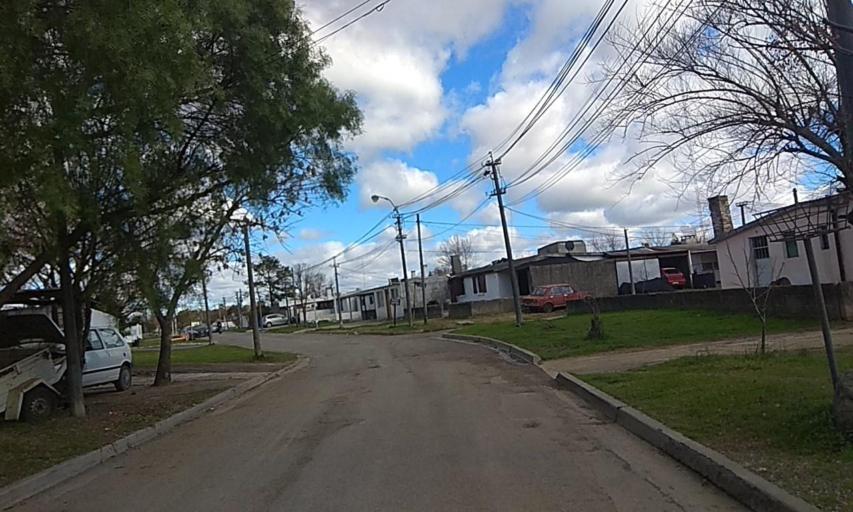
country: UY
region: Florida
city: Florida
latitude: -34.0952
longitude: -56.2339
